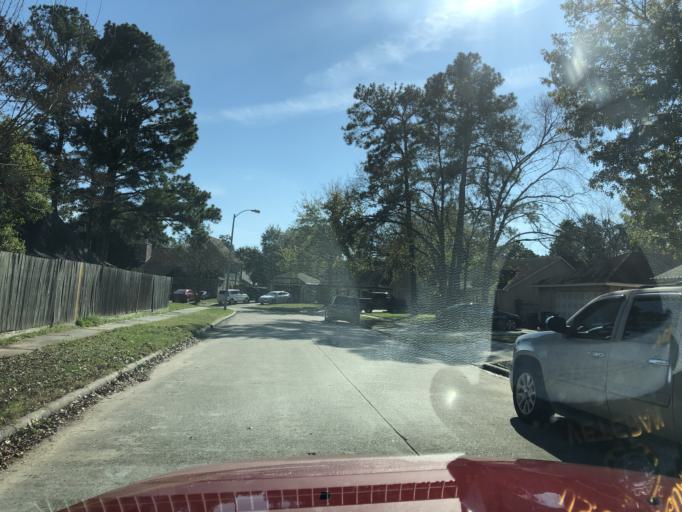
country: US
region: Texas
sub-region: Harris County
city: Tomball
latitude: 30.0196
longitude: -95.5585
